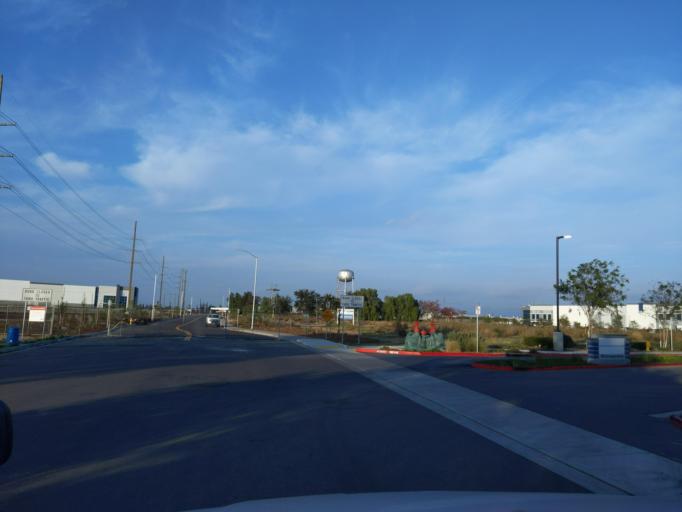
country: US
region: California
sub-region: San Joaquin County
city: Lathrop
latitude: 37.8046
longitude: -121.2920
